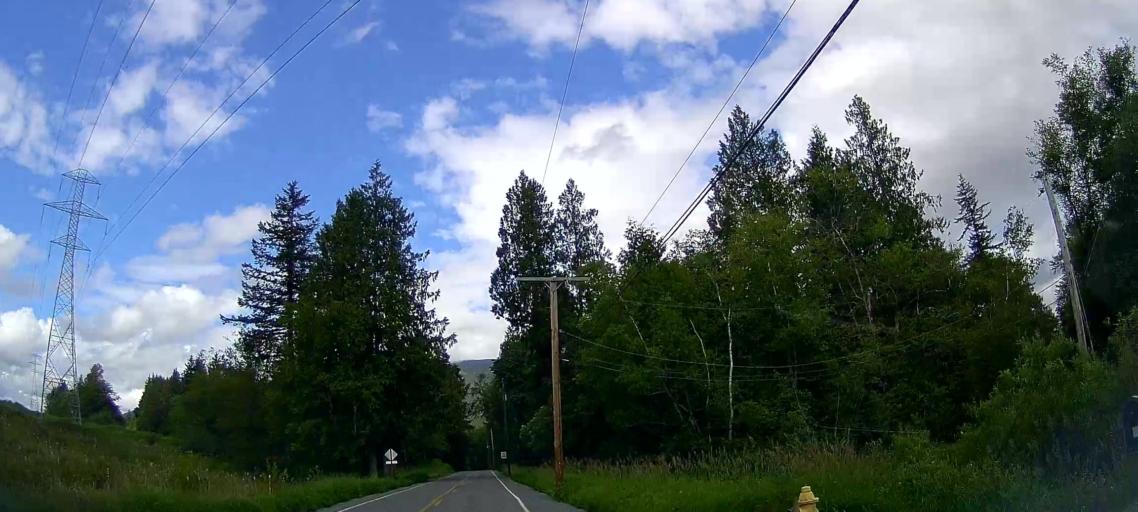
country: US
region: Washington
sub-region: Skagit County
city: Sedro-Woolley
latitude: 48.5435
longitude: -122.2179
